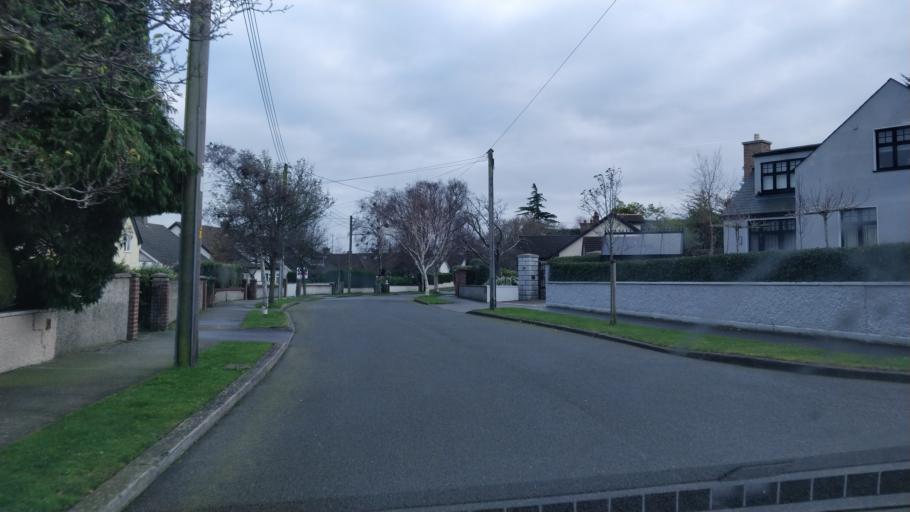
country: IE
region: Leinster
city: Foxrock
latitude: 53.2804
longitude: -6.1782
